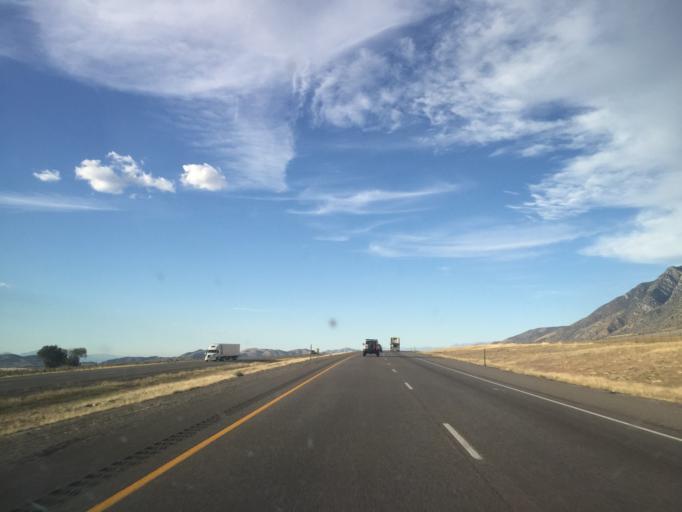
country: US
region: Utah
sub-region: Juab County
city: Mona
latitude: 39.7965
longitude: -111.8383
